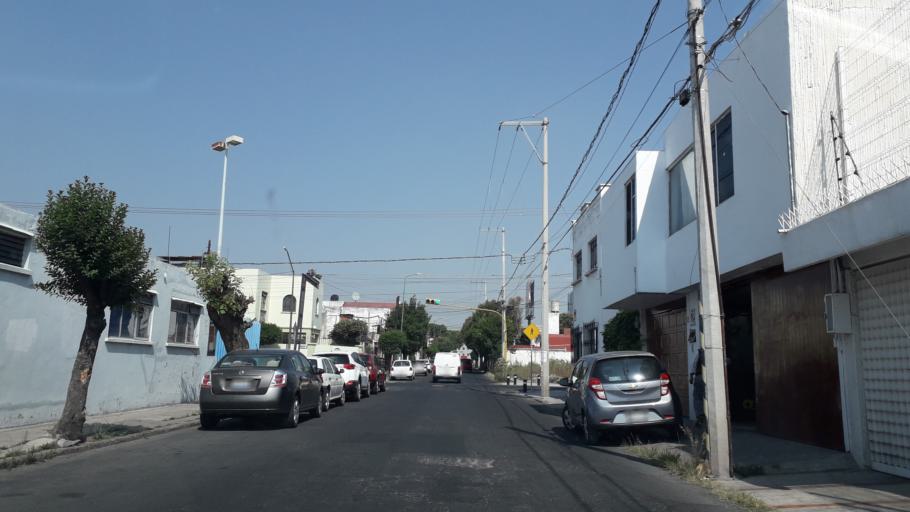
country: MX
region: Puebla
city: Puebla
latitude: 19.0341
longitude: -98.2121
